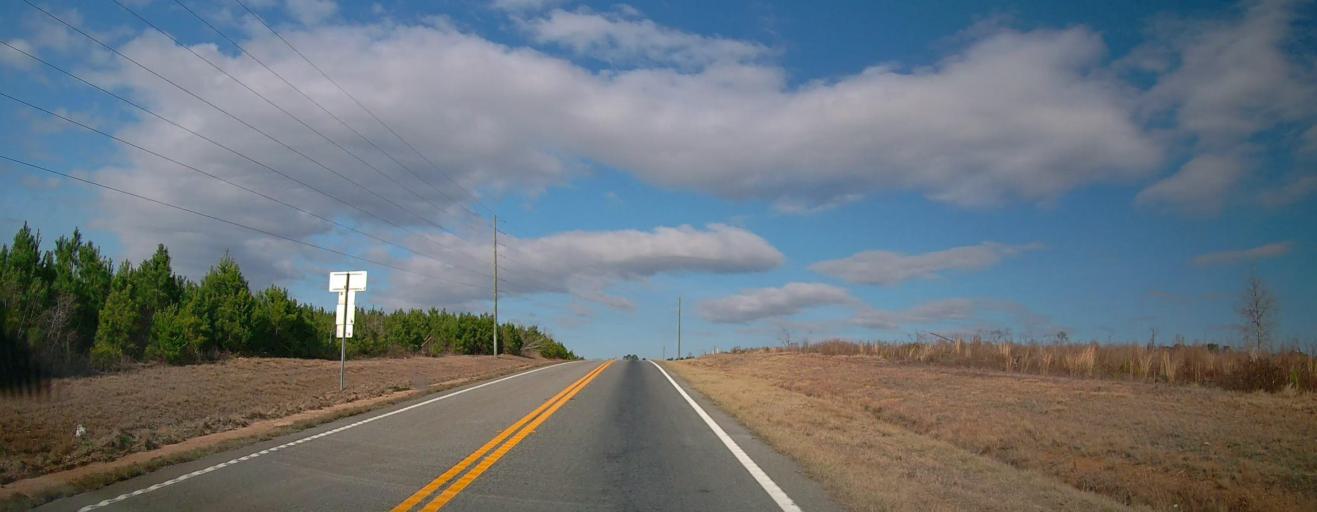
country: US
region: Georgia
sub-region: Taylor County
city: Butler
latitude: 32.4473
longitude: -84.3654
